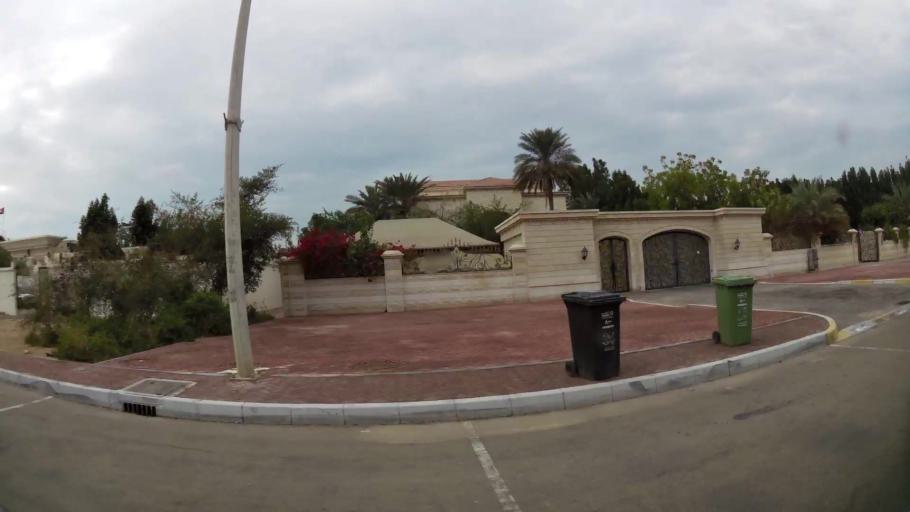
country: AE
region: Abu Dhabi
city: Abu Dhabi
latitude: 24.4354
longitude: 54.3981
